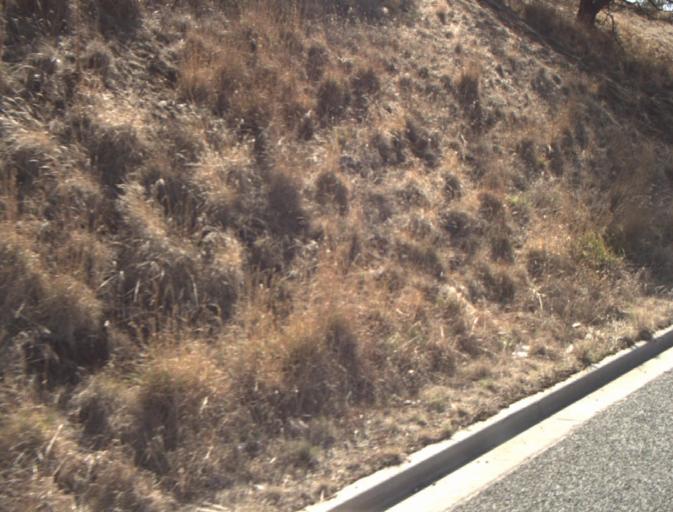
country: AU
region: Tasmania
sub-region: Launceston
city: Mayfield
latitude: -41.3701
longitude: 147.1095
